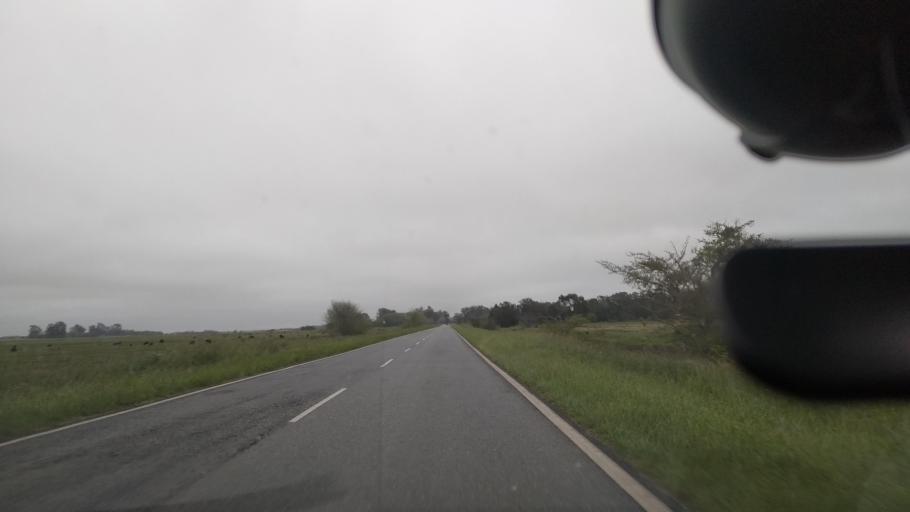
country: AR
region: Buenos Aires
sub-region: Partido de Magdalena
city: Magdalena
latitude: -35.2670
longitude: -57.6120
